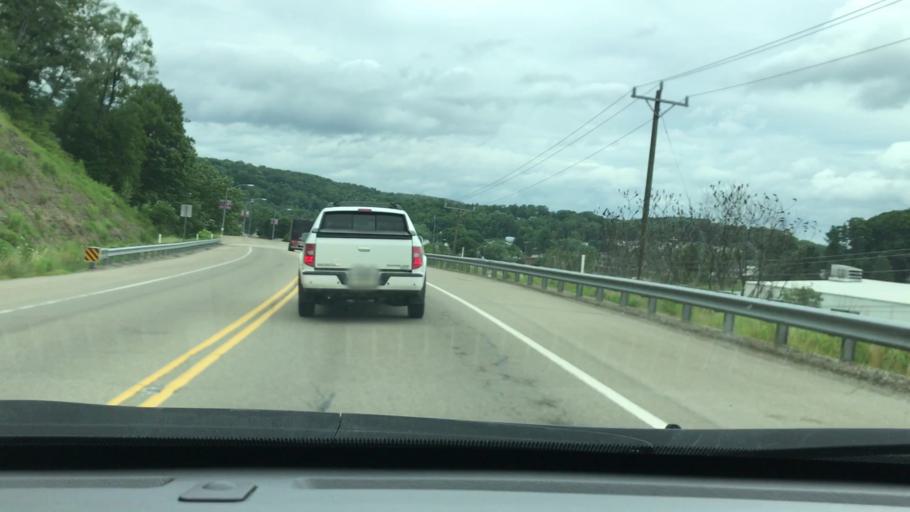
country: US
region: Pennsylvania
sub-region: Elk County
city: Johnsonburg
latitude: 41.4926
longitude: -78.6816
